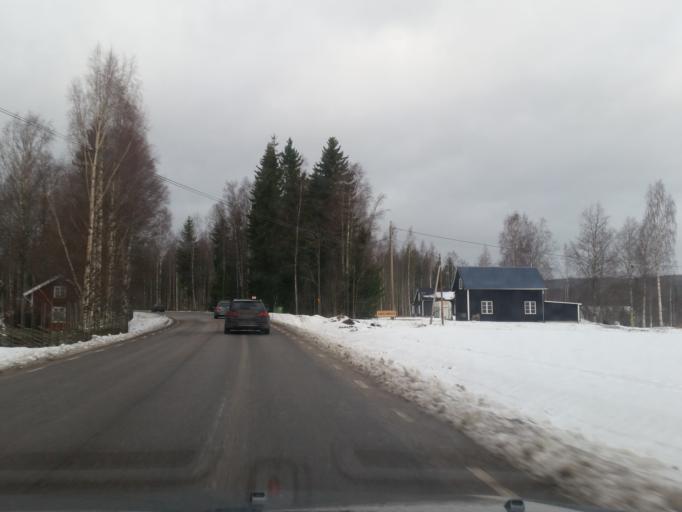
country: SE
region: Gaevleborg
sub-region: Sandvikens Kommun
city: Jarbo
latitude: 60.7631
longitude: 16.5139
